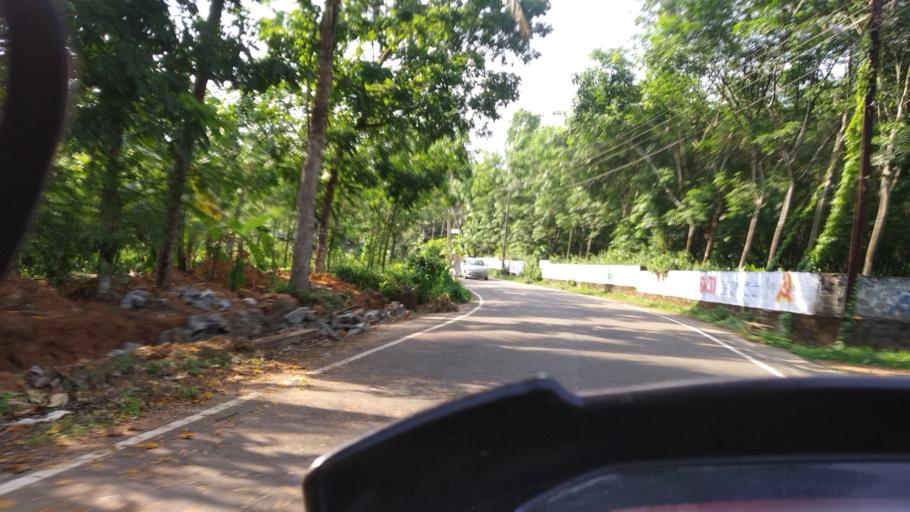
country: IN
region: Kerala
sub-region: Ernakulam
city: Piravam
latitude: 9.8350
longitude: 76.5401
